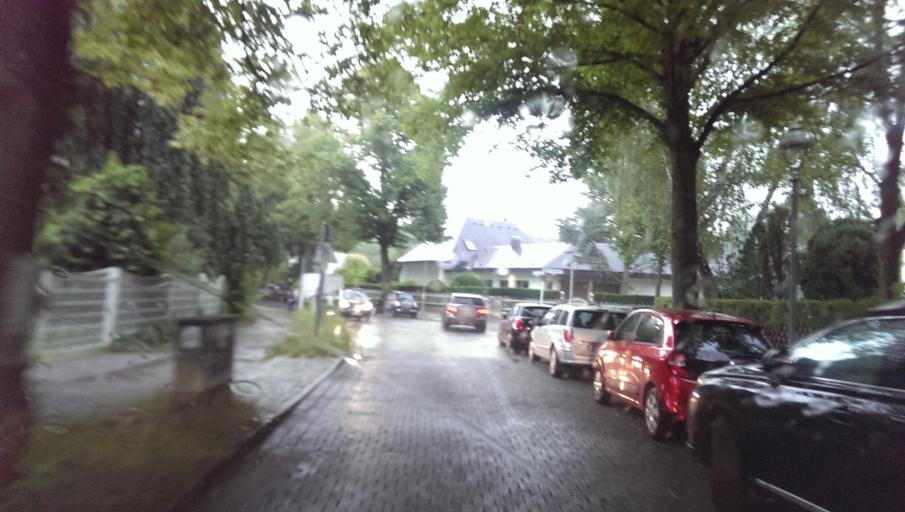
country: DE
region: Berlin
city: Zehlendorf Bezirk
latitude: 52.4249
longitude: 13.2706
